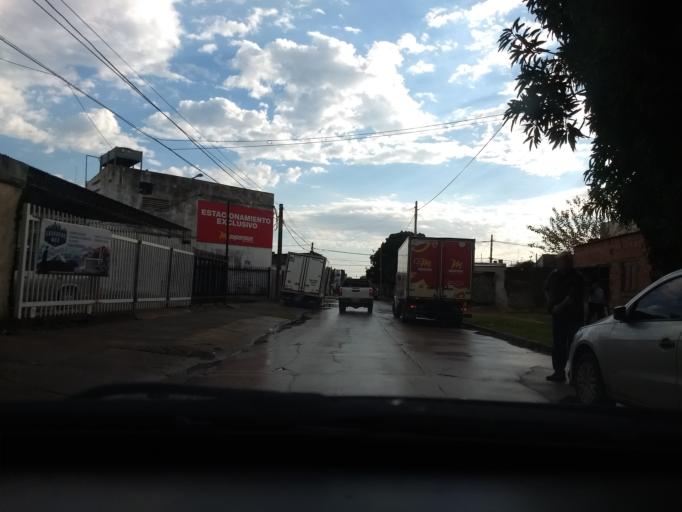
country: AR
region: Corrientes
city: Corrientes
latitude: -27.4783
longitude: -58.8289
